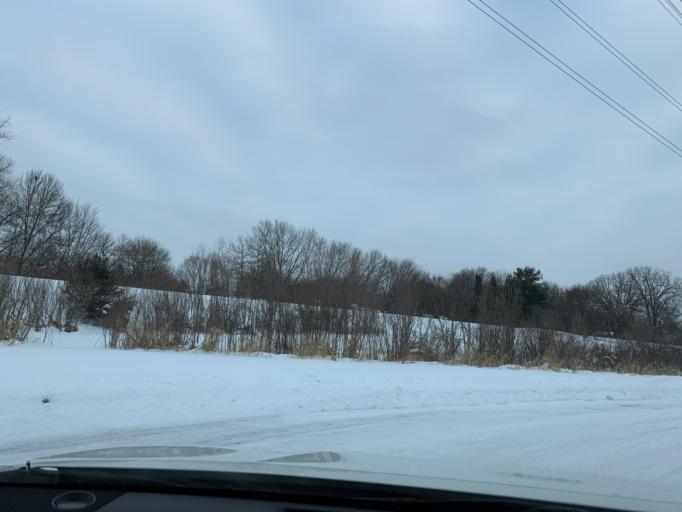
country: US
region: Minnesota
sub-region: Anoka County
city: Coon Rapids
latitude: 45.1604
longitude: -93.2946
